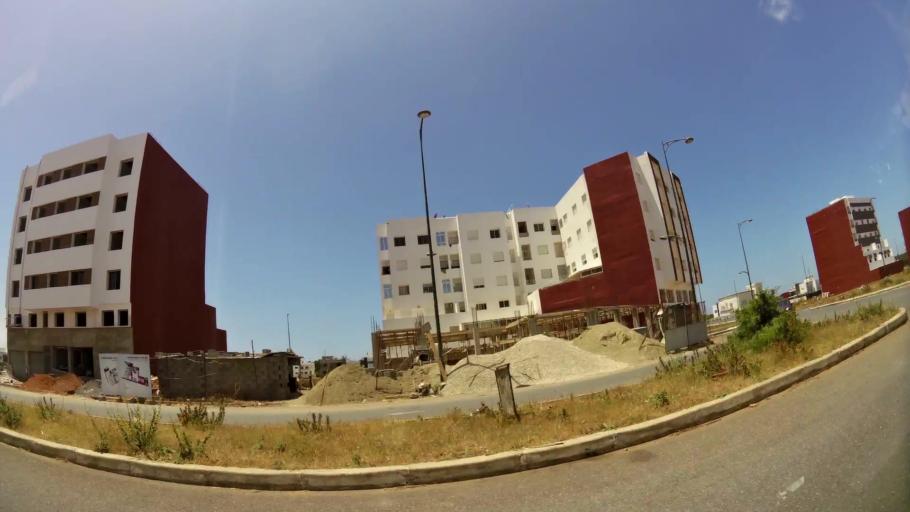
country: MA
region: Gharb-Chrarda-Beni Hssen
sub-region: Kenitra Province
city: Kenitra
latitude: 34.2673
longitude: -6.6270
